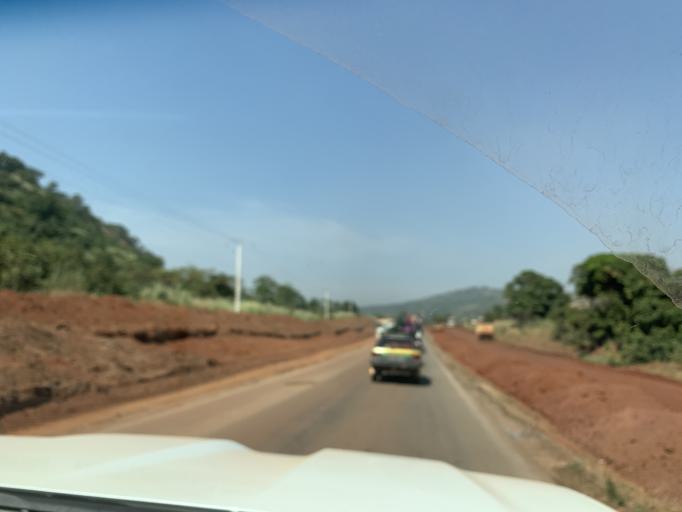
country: GN
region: Mamou
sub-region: Mamou Prefecture
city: Mamou
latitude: 10.2015
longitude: -12.4669
